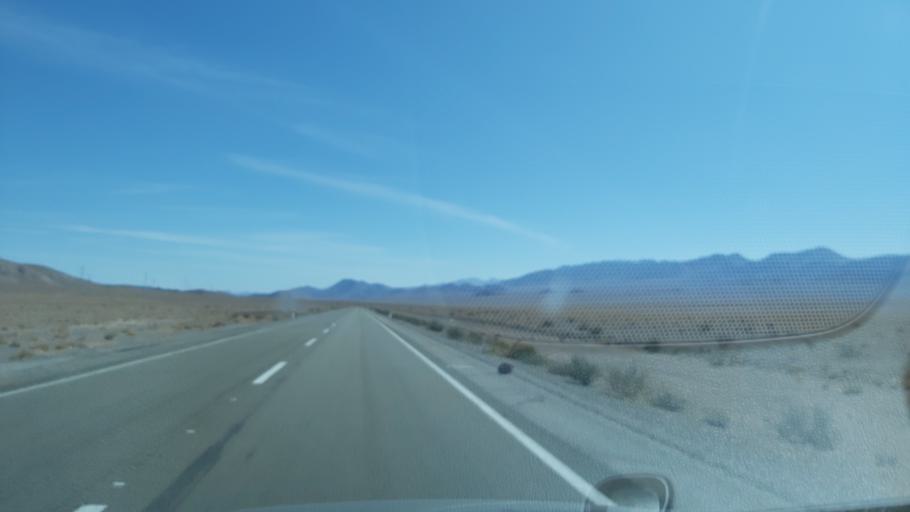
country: CL
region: Atacama
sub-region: Provincia de Chanaral
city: Diego de Almagro
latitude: -26.8650
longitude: -69.9056
